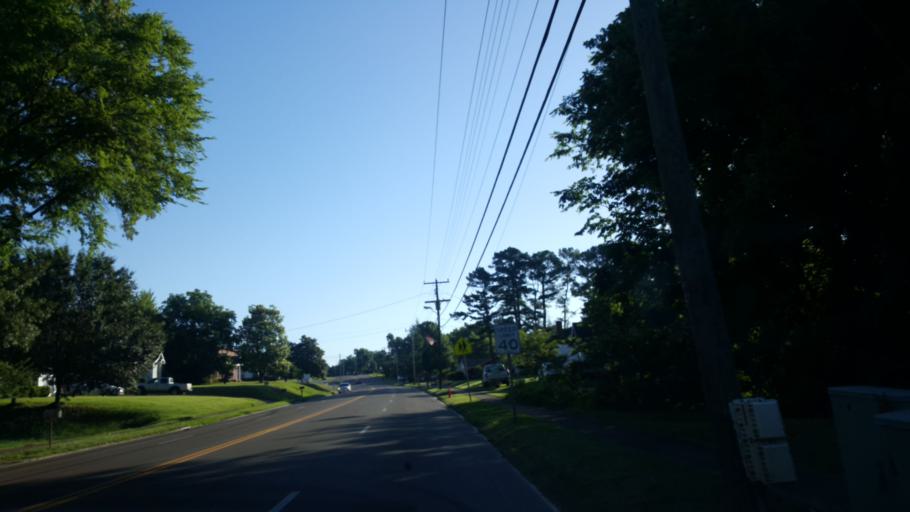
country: US
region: Tennessee
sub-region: Henderson County
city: Lexington
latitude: 35.6553
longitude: -88.3879
